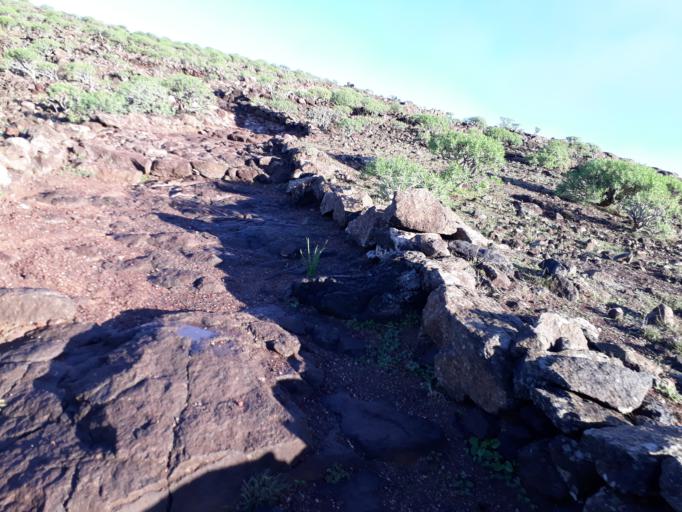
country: ES
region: Canary Islands
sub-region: Provincia de Santa Cruz de Tenerife
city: Vallehermosa
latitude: 28.1146
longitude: -17.3356
